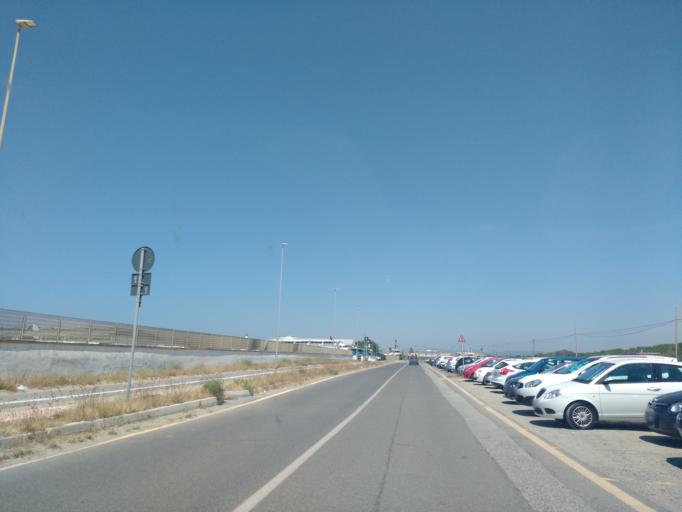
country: IT
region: Latium
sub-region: Citta metropolitana di Roma Capitale
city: Passo Oscuro
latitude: 41.8847
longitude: 12.1712
